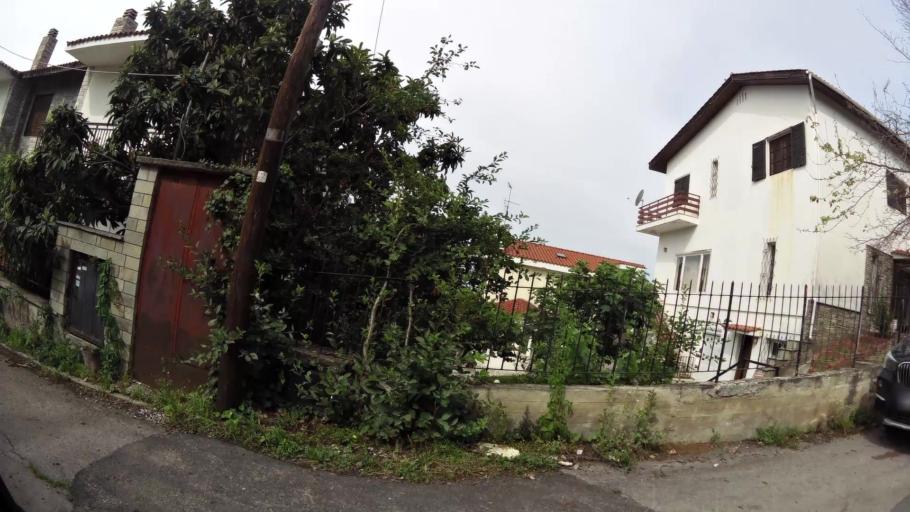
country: GR
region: Central Macedonia
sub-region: Nomos Thessalonikis
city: Panorama
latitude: 40.5883
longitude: 23.0206
